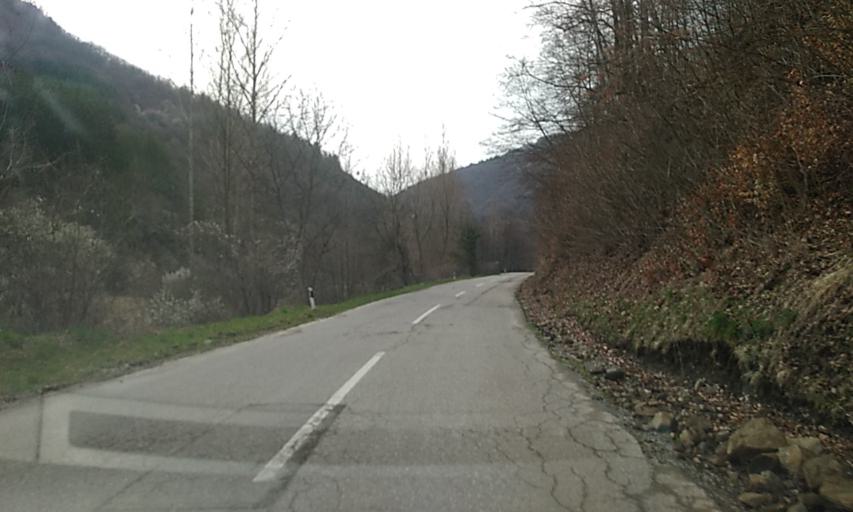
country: RS
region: Central Serbia
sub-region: Pcinjski Okrug
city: Bosilegrad
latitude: 42.5338
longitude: 22.4238
